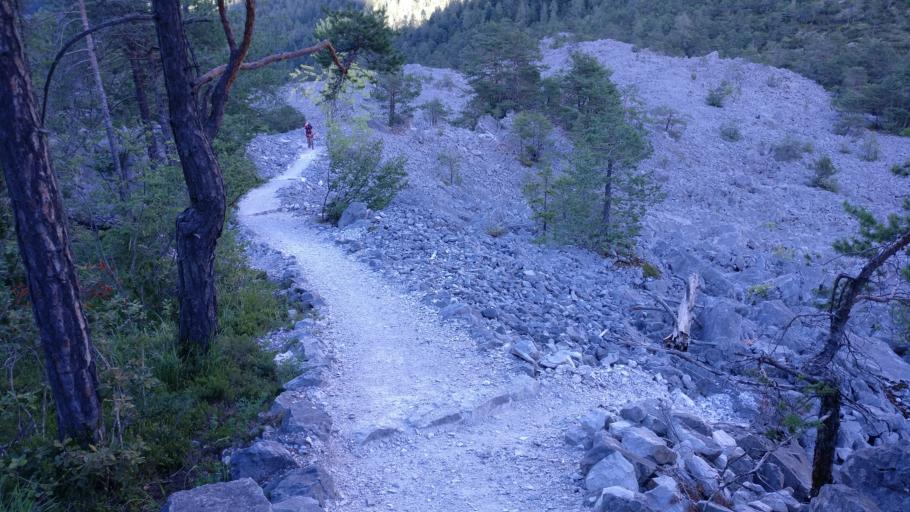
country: IT
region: Trentino-Alto Adige
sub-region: Provincia di Trento
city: Terres
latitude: 46.2816
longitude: 10.9659
